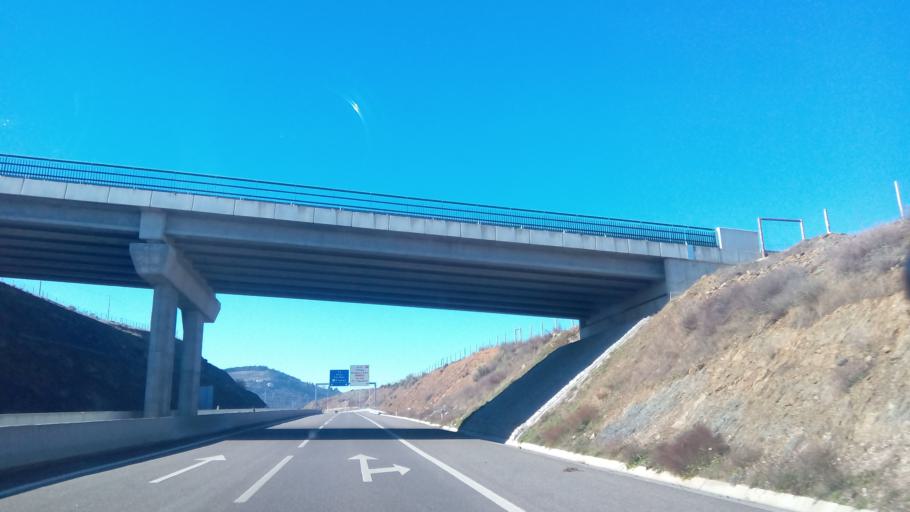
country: PT
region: Braganca
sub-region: Braganca Municipality
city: Braganca
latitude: 41.7909
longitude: -6.7144
